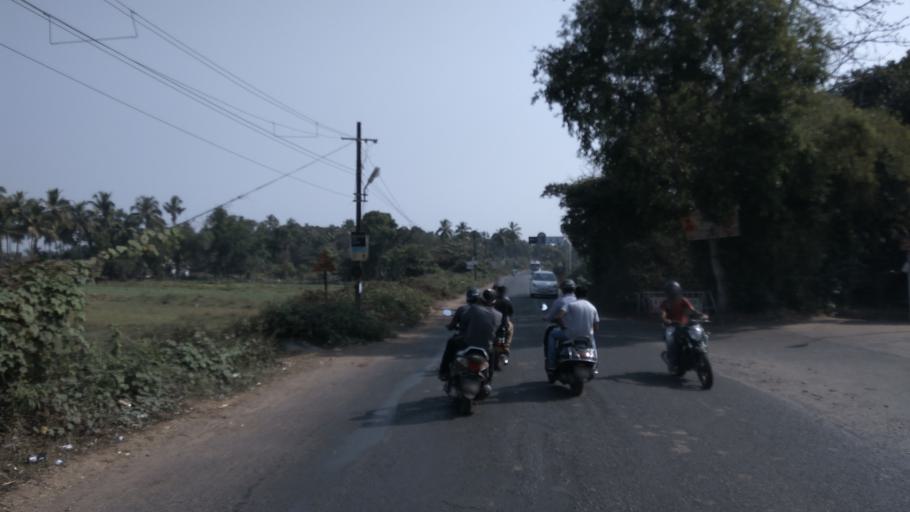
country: IN
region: Goa
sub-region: North Goa
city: Saligao
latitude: 15.5441
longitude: 73.7804
